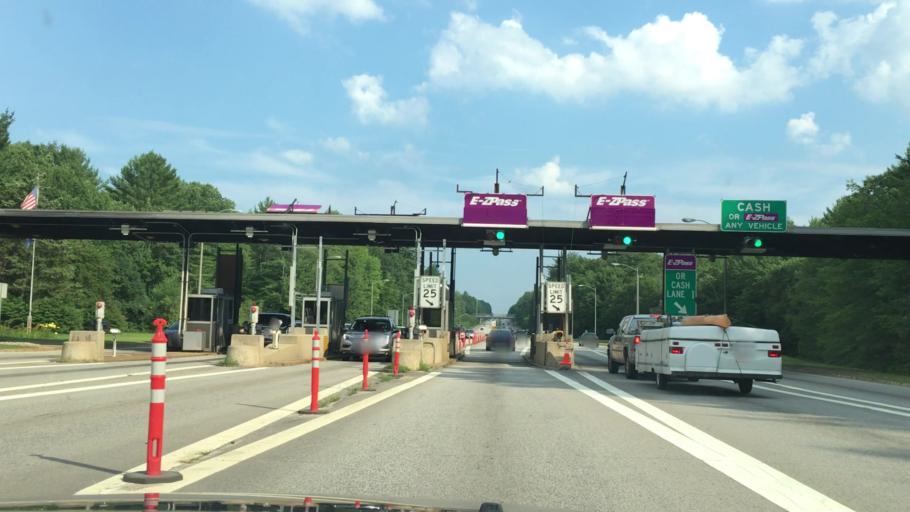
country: US
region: New Hampshire
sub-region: Strafford County
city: Rochester
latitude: 43.2738
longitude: -70.9634
